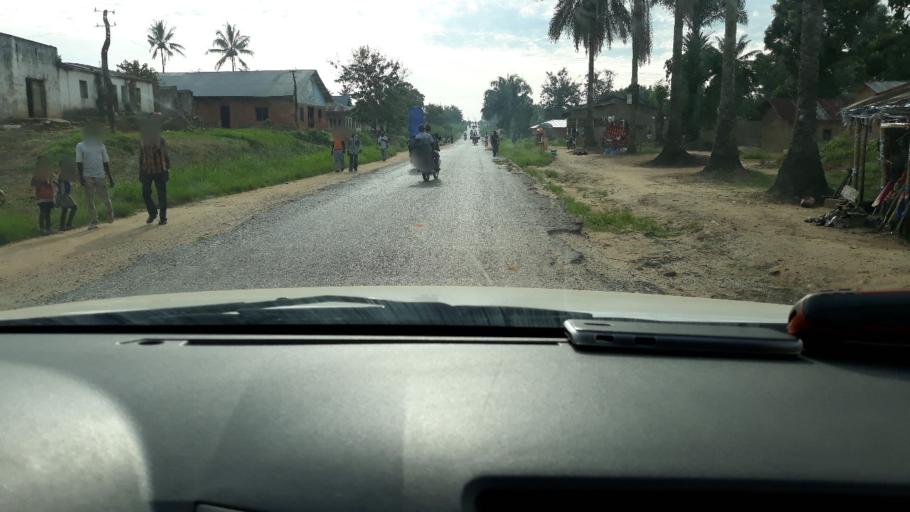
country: CD
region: Maniema
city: Kindu
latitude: -2.9518
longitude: 25.9437
